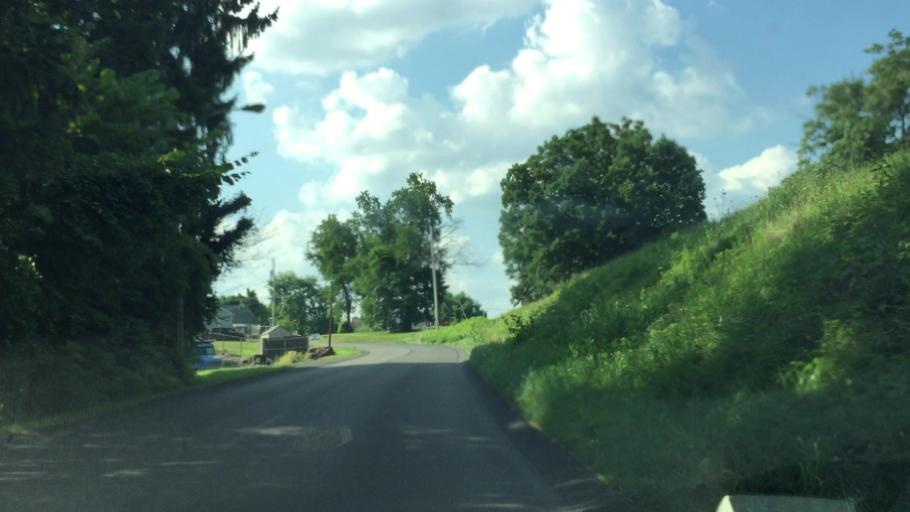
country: US
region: Pennsylvania
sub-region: Allegheny County
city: Coraopolis
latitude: 40.5098
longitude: -80.1716
